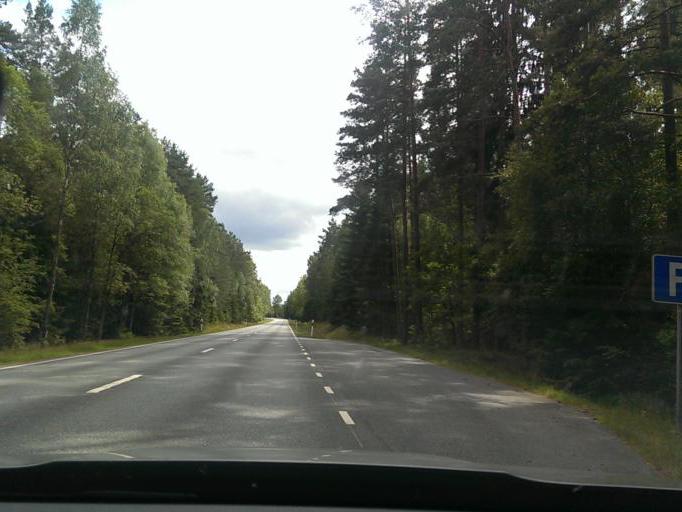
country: SE
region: Joenkoeping
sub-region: Varnamo Kommun
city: Varnamo
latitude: 57.2722
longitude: 13.9700
